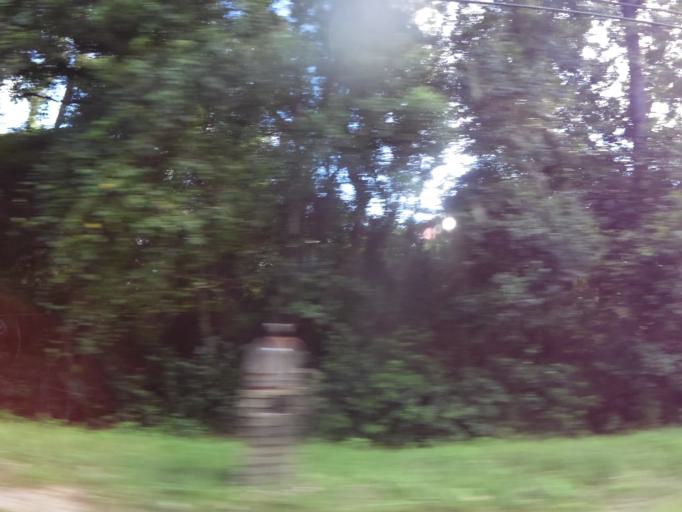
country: US
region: Florida
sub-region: Duval County
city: Jacksonville
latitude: 30.3285
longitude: -81.7830
